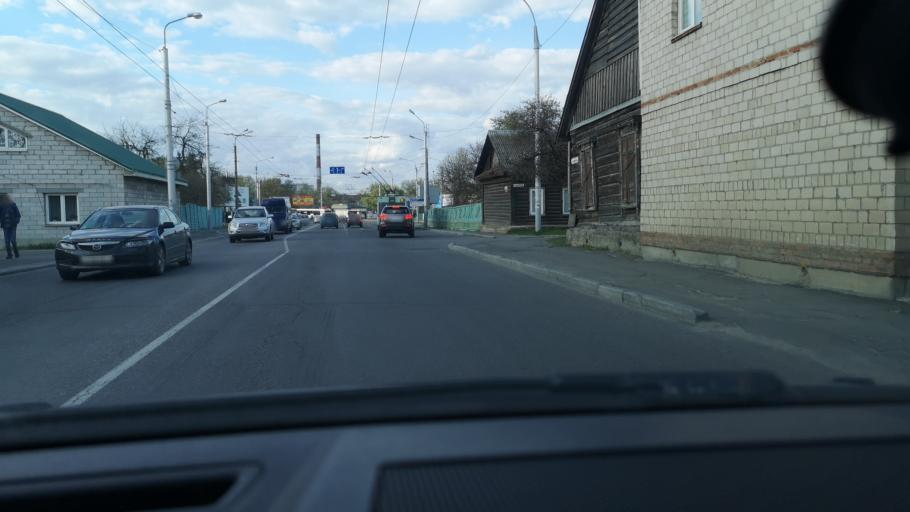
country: BY
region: Gomel
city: Gomel
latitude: 52.4387
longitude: 30.9776
